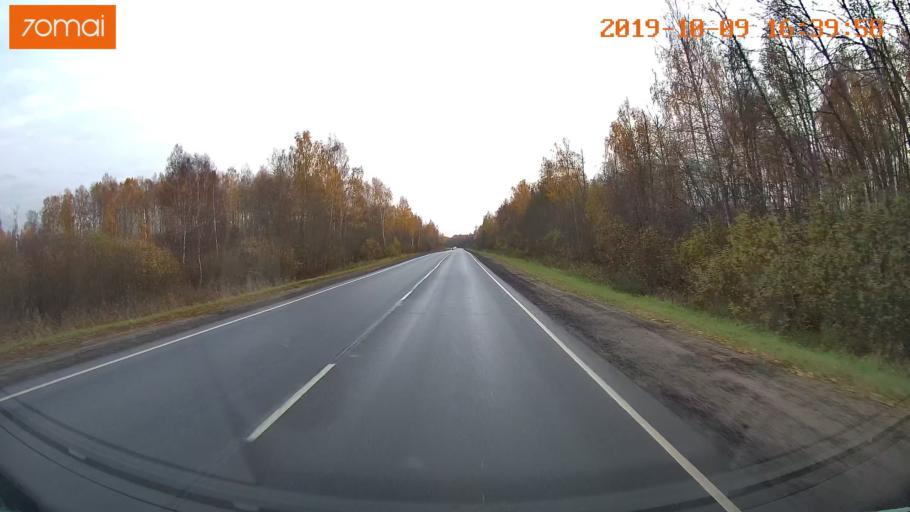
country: RU
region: Kostroma
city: Volgorechensk
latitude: 57.4904
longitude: 41.0548
